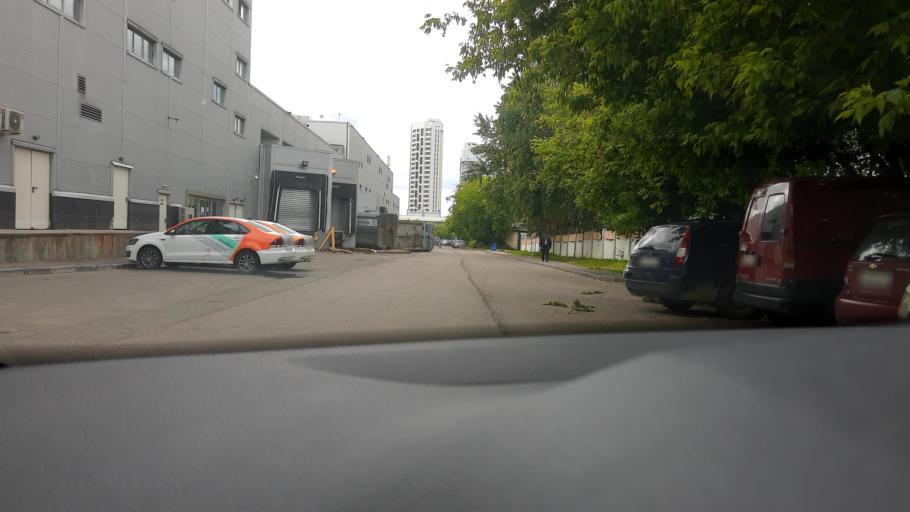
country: RU
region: Moscow
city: Rublevo
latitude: 55.7667
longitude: 37.3827
